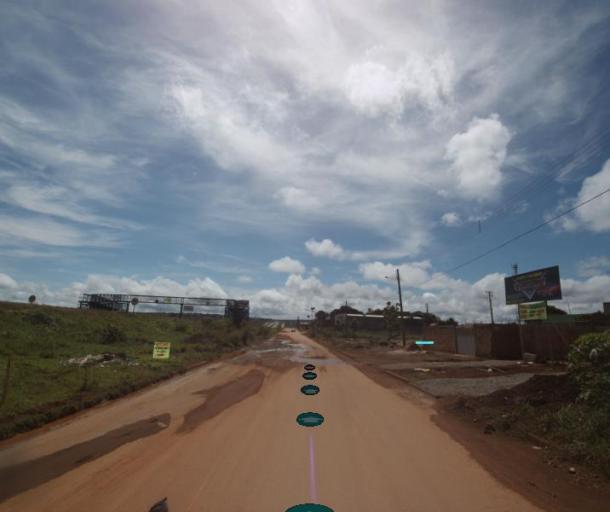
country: BR
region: Federal District
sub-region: Brasilia
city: Brasilia
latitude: -15.7543
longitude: -48.3277
